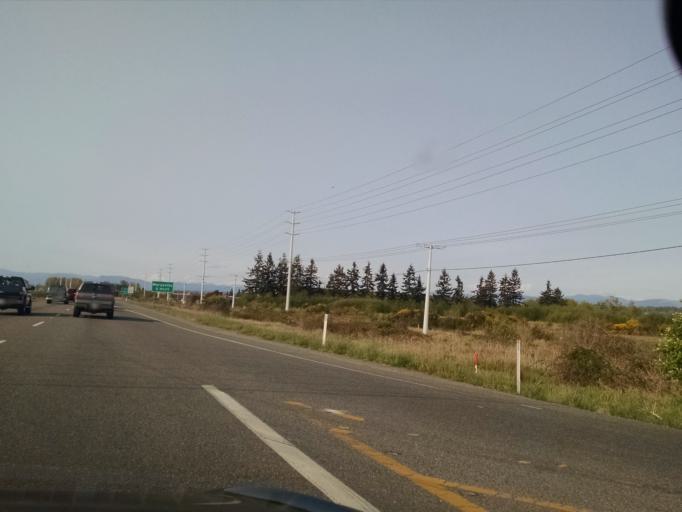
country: US
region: Washington
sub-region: Snohomish County
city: Marysville
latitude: 48.0230
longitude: -122.1857
